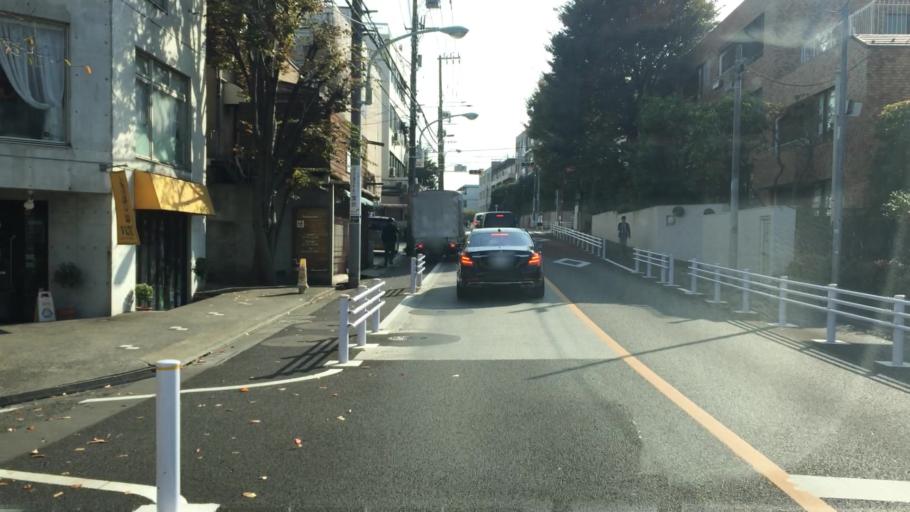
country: JP
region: Tokyo
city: Tokyo
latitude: 35.6212
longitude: 139.6670
